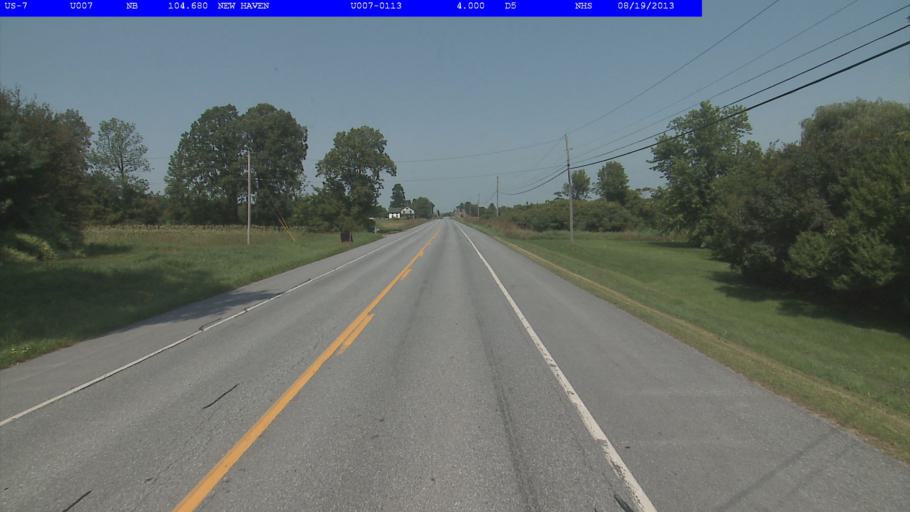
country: US
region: Vermont
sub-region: Addison County
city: Middlebury (village)
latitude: 44.1030
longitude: -73.1735
